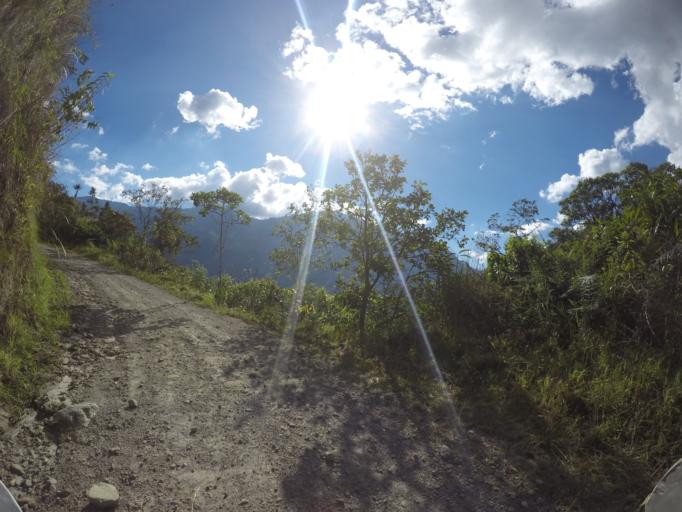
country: CO
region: Tolima
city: Cajamarca
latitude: 4.5036
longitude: -75.3943
